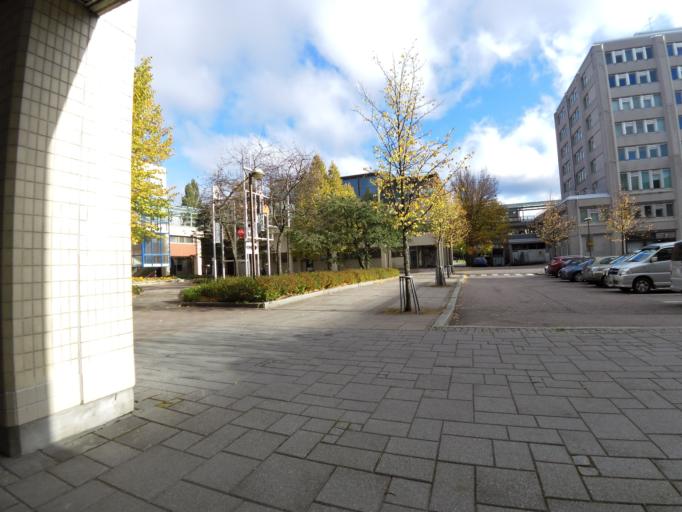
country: FI
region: Uusimaa
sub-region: Helsinki
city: Espoo
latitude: 60.2058
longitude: 24.6540
